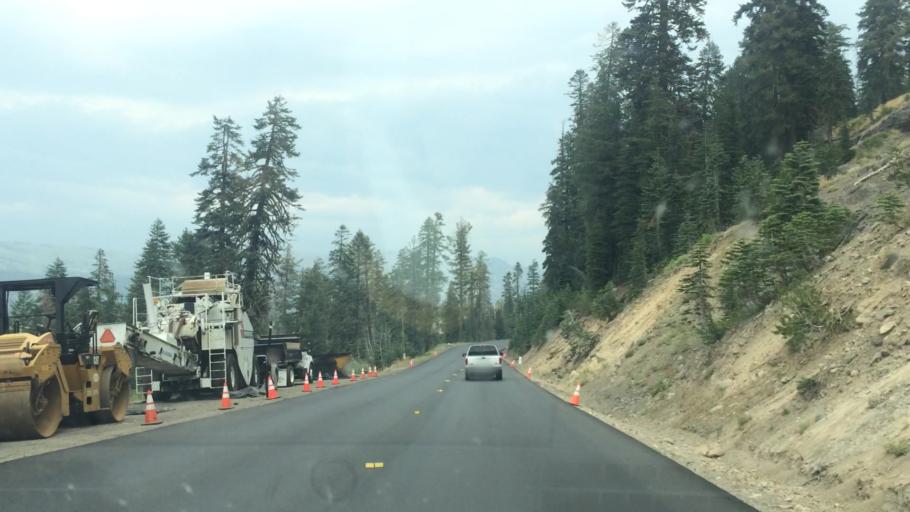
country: US
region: California
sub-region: El Dorado County
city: South Lake Tahoe
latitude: 38.7033
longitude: -120.0933
